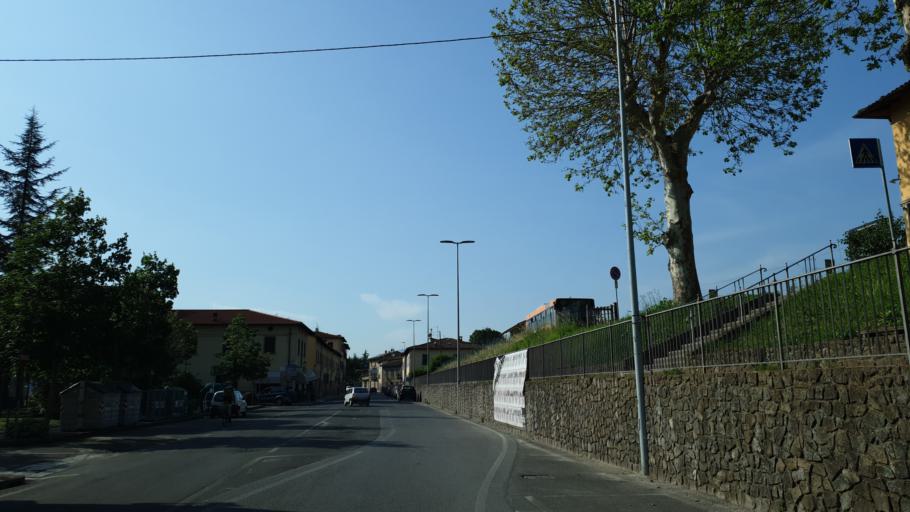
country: IT
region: Tuscany
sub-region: Province of Arezzo
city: Ponte a Poppi
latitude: 43.7300
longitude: 11.7678
